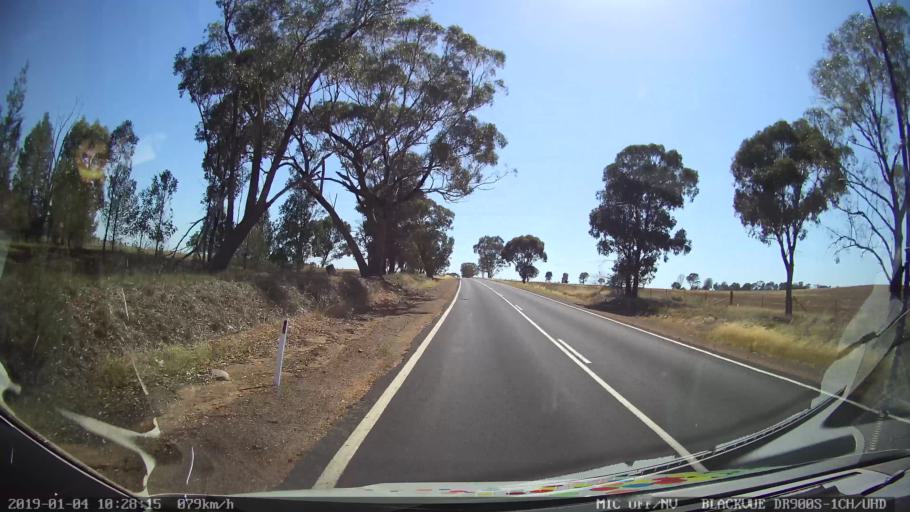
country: AU
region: New South Wales
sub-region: Cabonne
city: Canowindra
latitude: -33.3644
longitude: 148.6075
